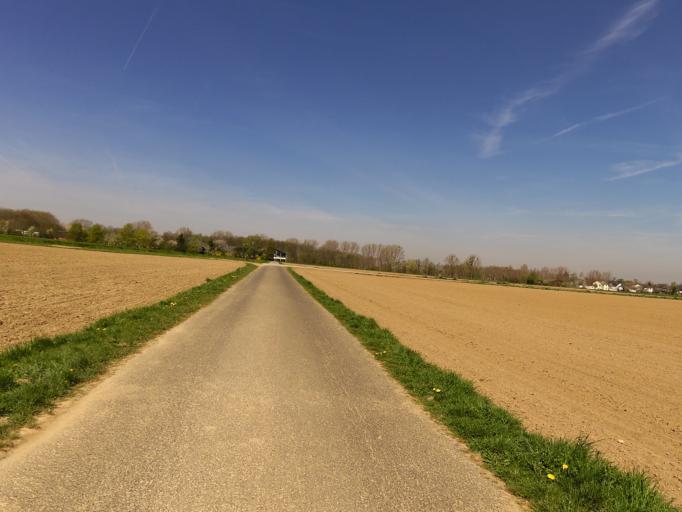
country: DE
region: North Rhine-Westphalia
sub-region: Regierungsbezirk Koln
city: Rheinbach
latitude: 50.6391
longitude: 6.8810
